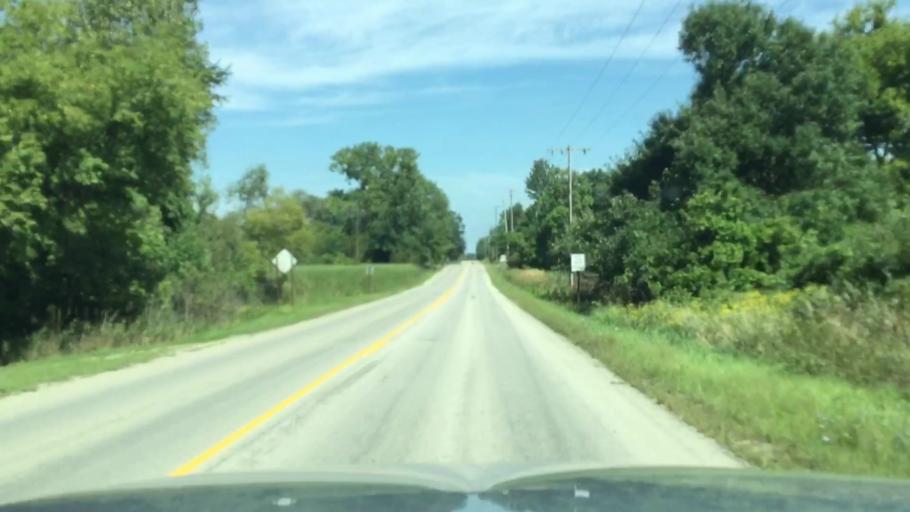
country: US
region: Michigan
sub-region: Lenawee County
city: Manitou Beach-Devils Lake
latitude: 42.0049
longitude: -84.2760
